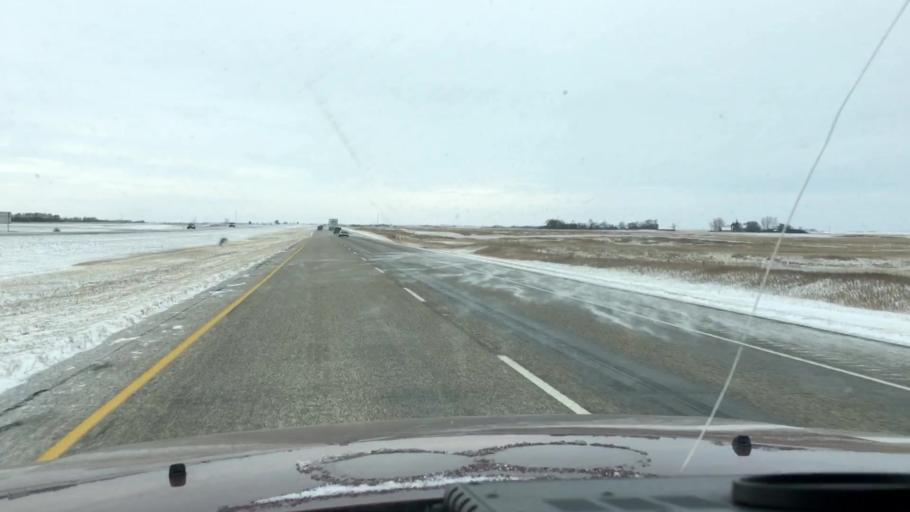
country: CA
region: Saskatchewan
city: Saskatoon
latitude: 51.6265
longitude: -106.4233
